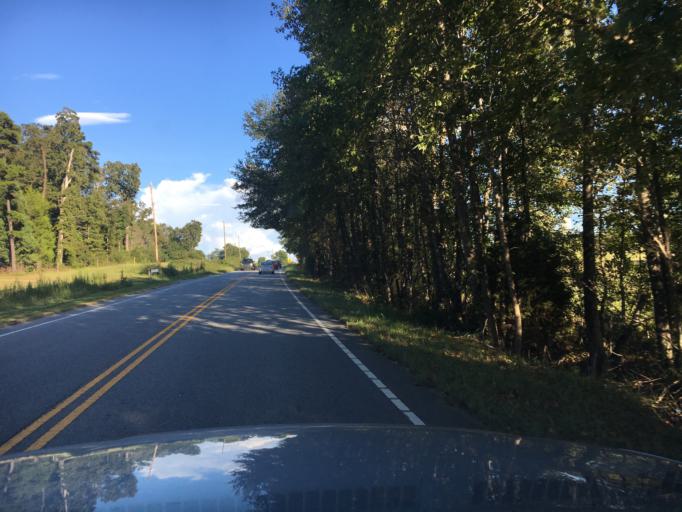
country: US
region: South Carolina
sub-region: Spartanburg County
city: Woodruff
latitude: 34.7893
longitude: -82.1183
